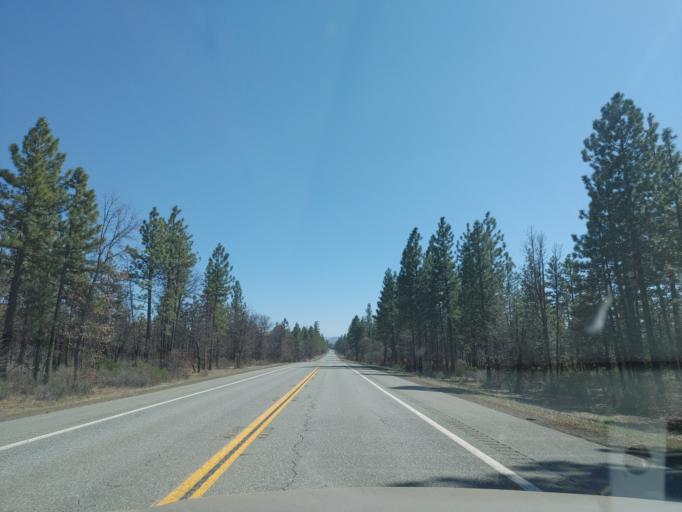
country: US
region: California
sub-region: Shasta County
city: Burney
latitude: 40.9549
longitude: -121.6132
